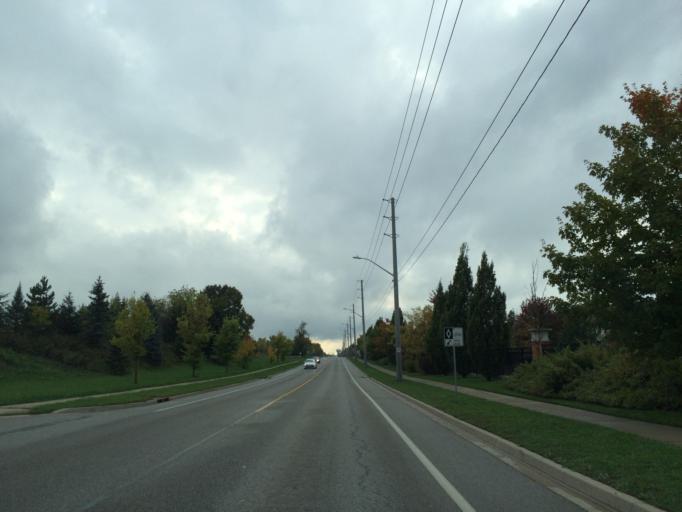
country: CA
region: Ontario
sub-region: Wellington County
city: Guelph
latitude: 43.5106
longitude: -80.1754
